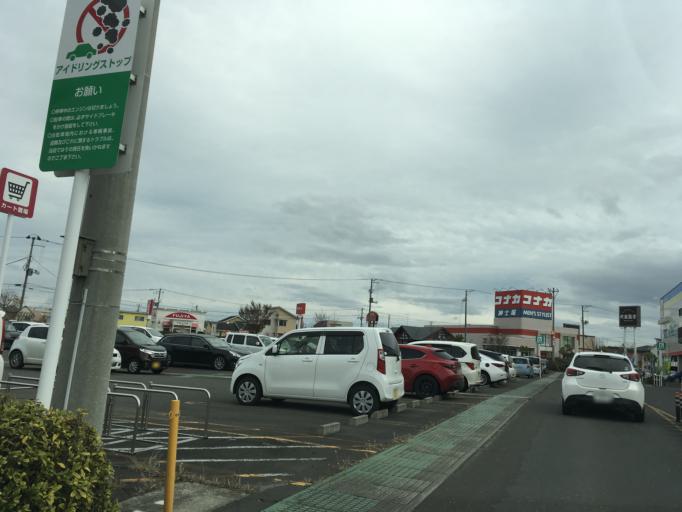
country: JP
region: Miyagi
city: Wakuya
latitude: 38.6845
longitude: 141.1851
